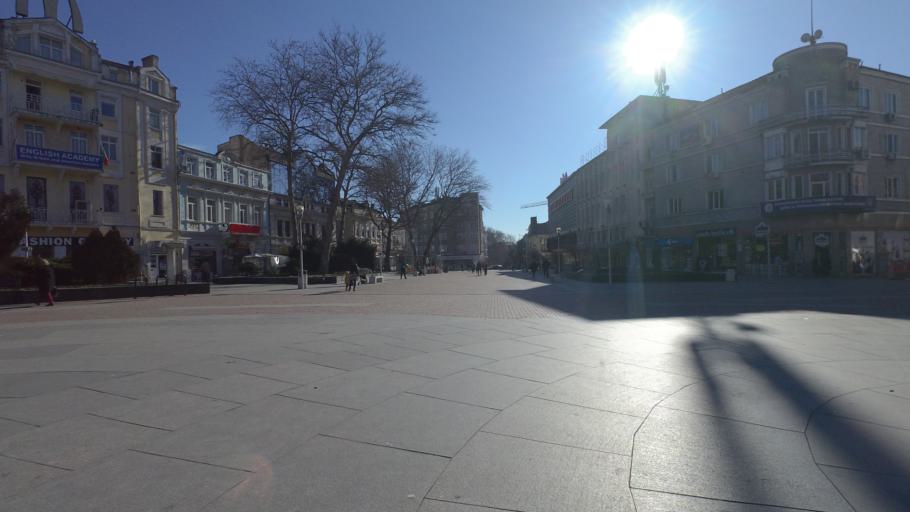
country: BG
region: Varna
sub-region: Obshtina Varna
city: Varna
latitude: 43.2036
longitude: 27.9125
